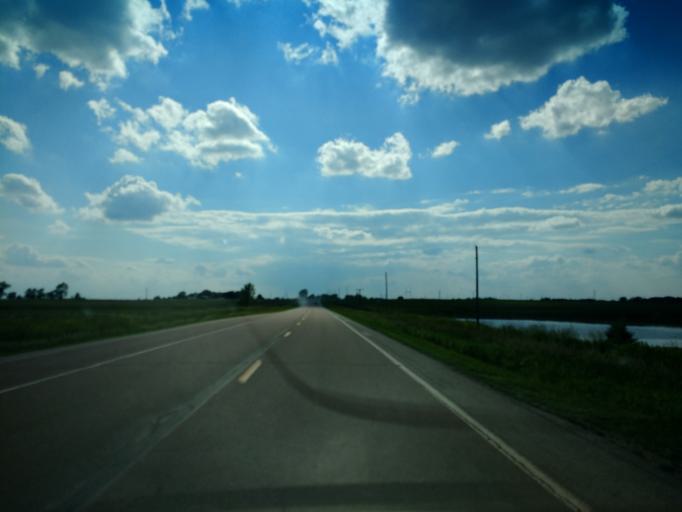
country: US
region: Iowa
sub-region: Clay County
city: Spencer
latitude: 43.1837
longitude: -95.2301
